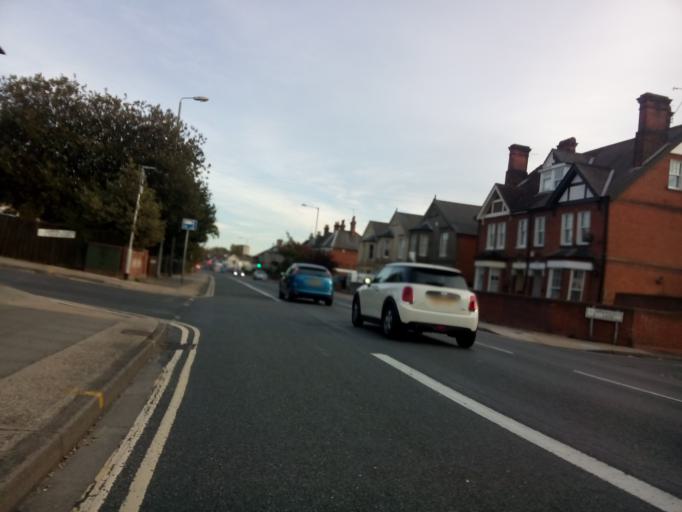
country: GB
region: England
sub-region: Suffolk
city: Ipswich
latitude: 52.0695
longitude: 1.1350
